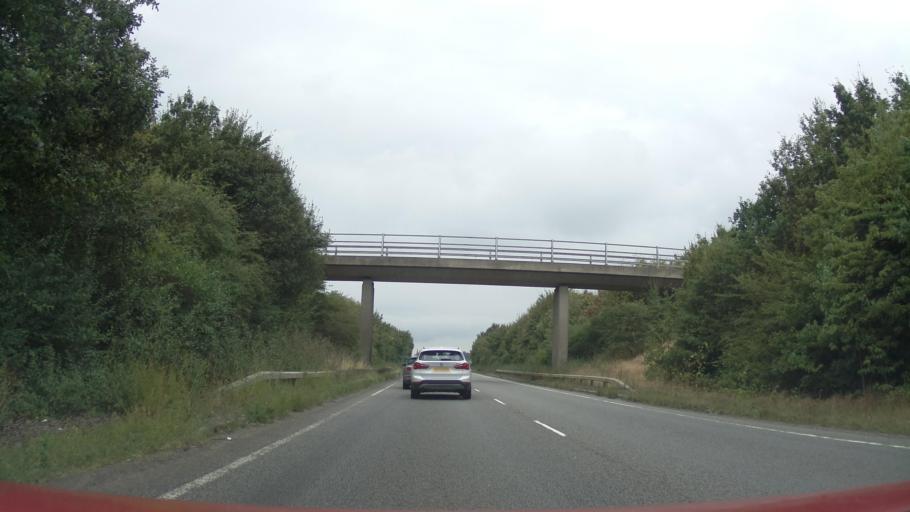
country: GB
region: England
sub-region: Nottinghamshire
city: South Collingham
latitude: 53.0924
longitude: -0.7693
